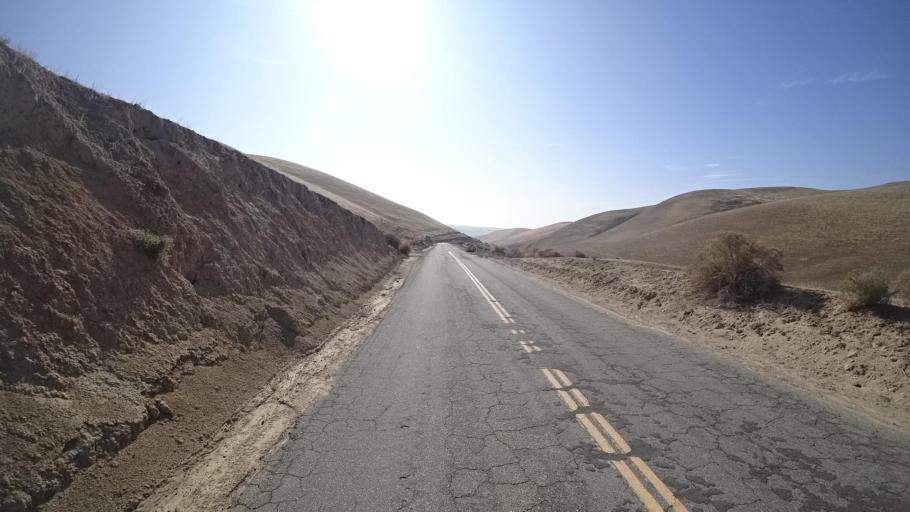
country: US
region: California
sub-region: Kern County
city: Oildale
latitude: 35.4585
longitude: -118.8276
